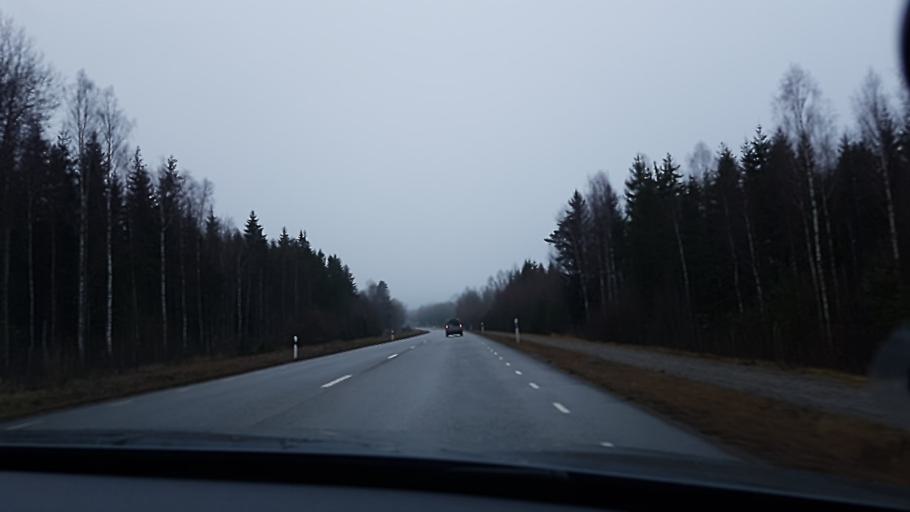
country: SE
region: Vaestra Goetaland
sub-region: Gullspangs Kommun
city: Gullspang
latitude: 58.8562
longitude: 14.0010
